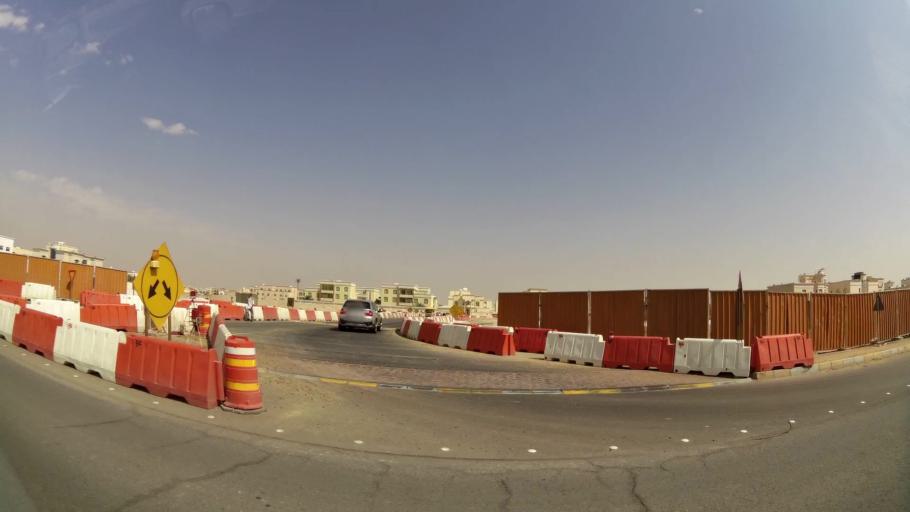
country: AE
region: Abu Dhabi
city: Abu Dhabi
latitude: 24.3322
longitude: 54.5390
